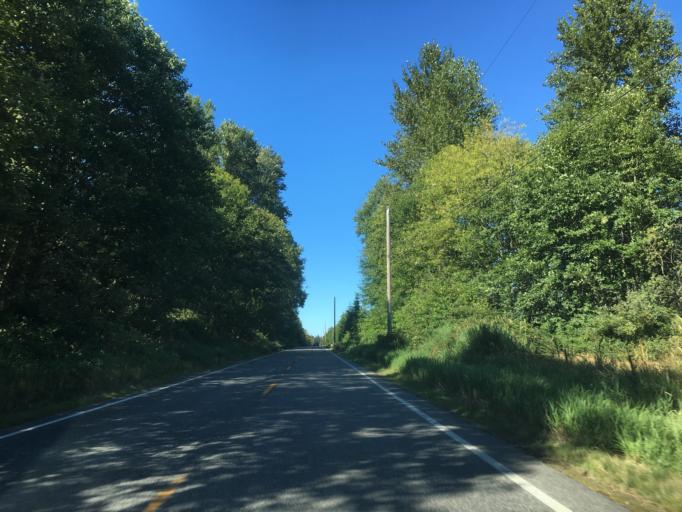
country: US
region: Washington
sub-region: Skagit County
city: Sedro-Woolley
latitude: 48.6073
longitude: -122.2309
